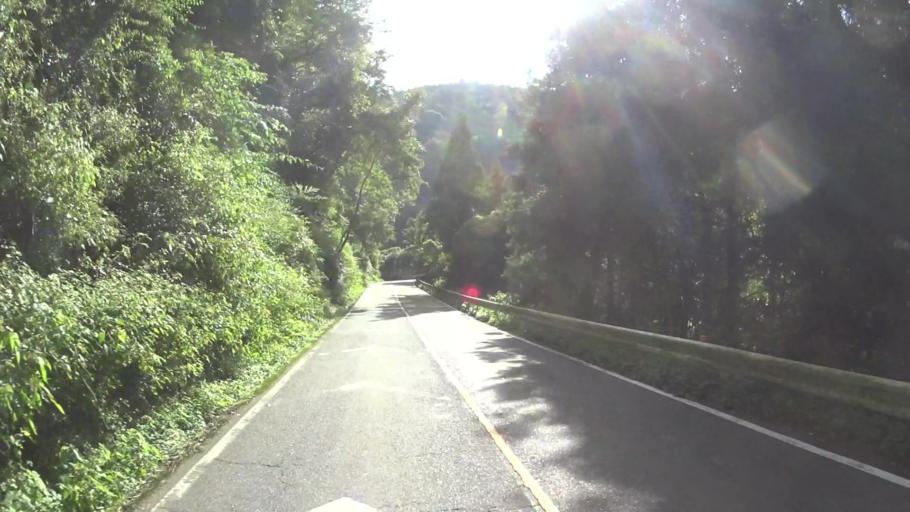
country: JP
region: Kyoto
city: Uji
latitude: 34.9040
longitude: 135.8675
